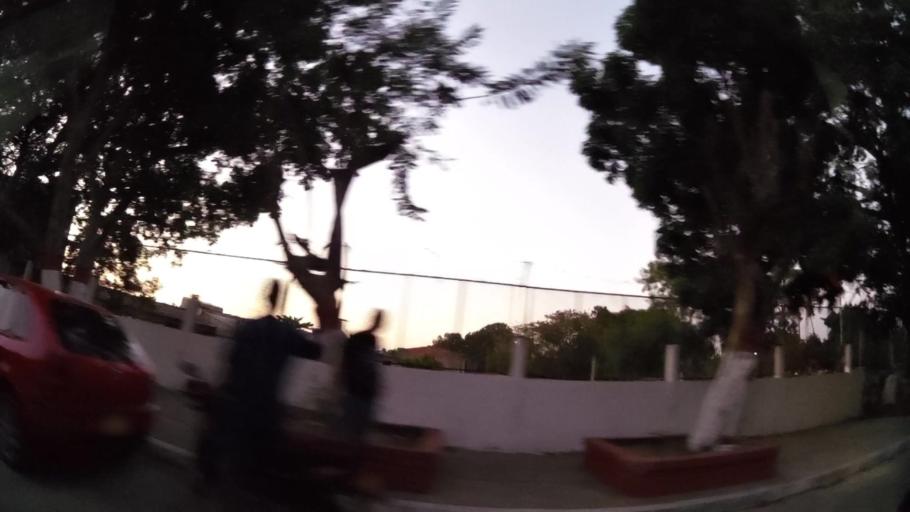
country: CO
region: Bolivar
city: Cartagena
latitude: 10.3876
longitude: -75.4947
